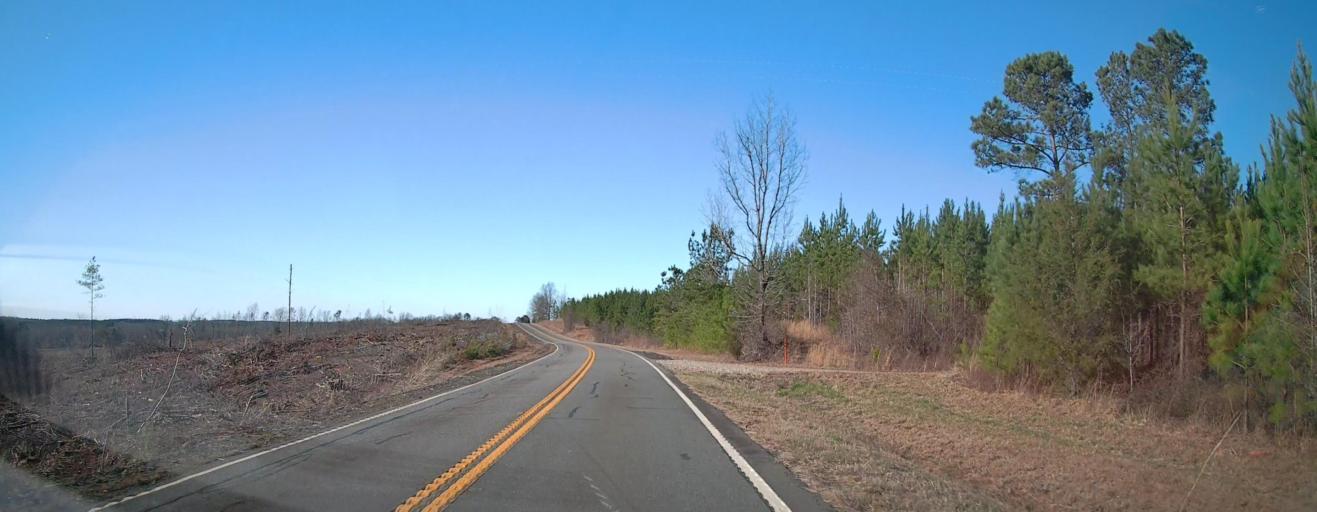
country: US
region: Georgia
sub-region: Talbot County
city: Talbotton
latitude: 32.6618
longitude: -84.4607
